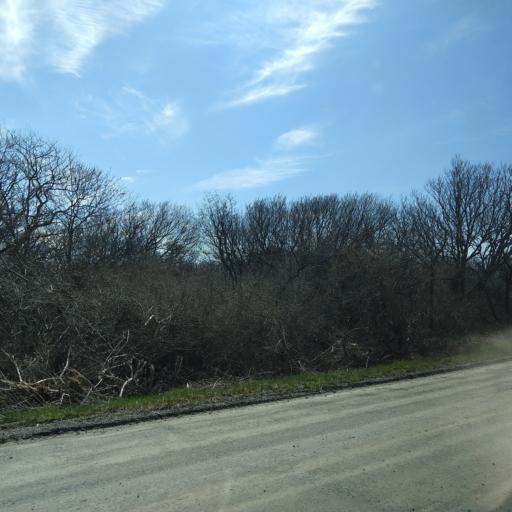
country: US
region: Massachusetts
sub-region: Essex County
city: Ipswich
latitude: 42.7106
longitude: -70.7760
